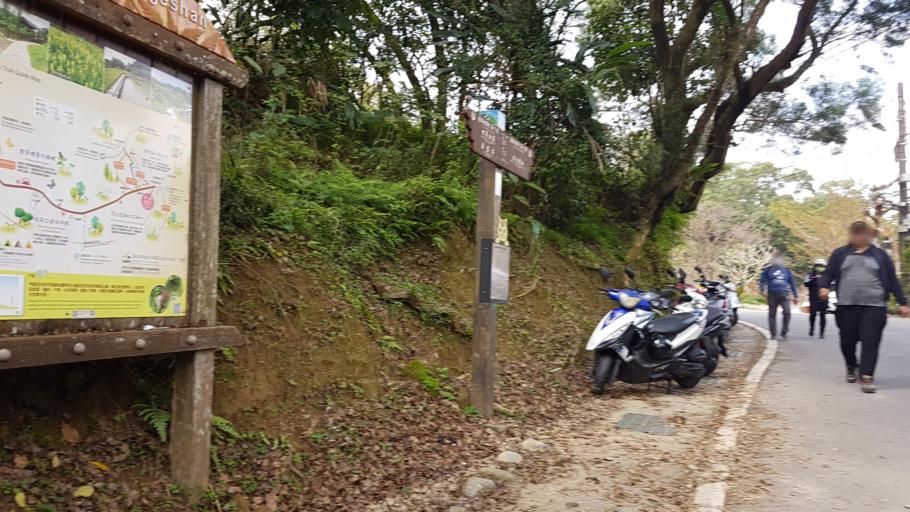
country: TW
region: Taipei
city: Taipei
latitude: 24.9708
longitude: 121.5805
